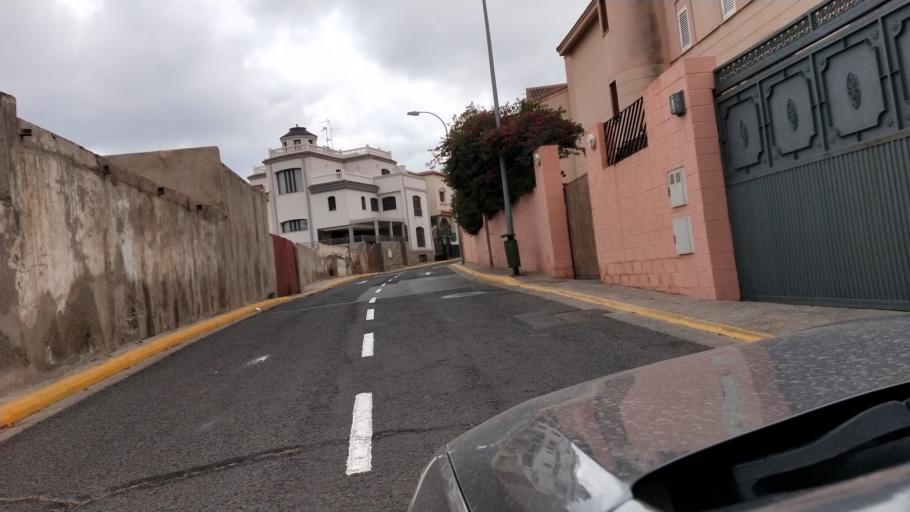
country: ES
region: Melilla
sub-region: Melilla
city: Melilla
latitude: 35.2903
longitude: -2.9552
